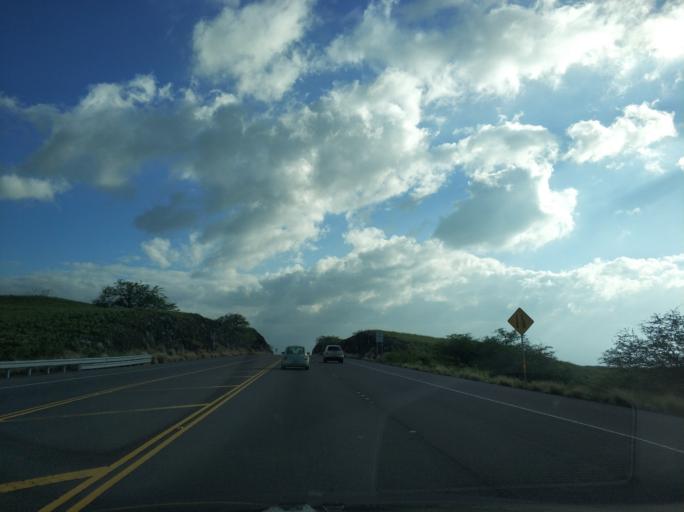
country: US
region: Hawaii
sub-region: Hawaii County
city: Waikoloa
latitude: 19.9905
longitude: -155.8176
